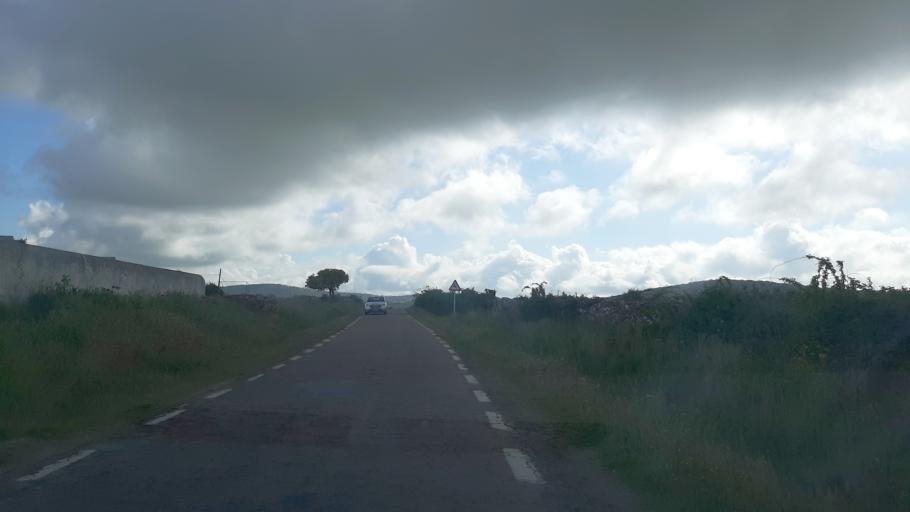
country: ES
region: Castille and Leon
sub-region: Provincia de Salamanca
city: Narros de Matalayegua
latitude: 40.7001
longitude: -5.9244
